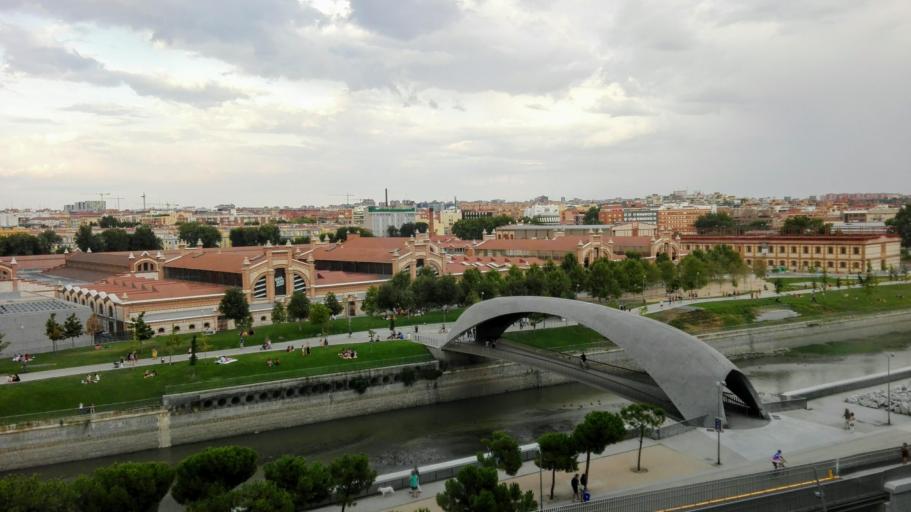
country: ES
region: Madrid
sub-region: Provincia de Madrid
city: Usera
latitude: 40.3908
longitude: -3.7010
